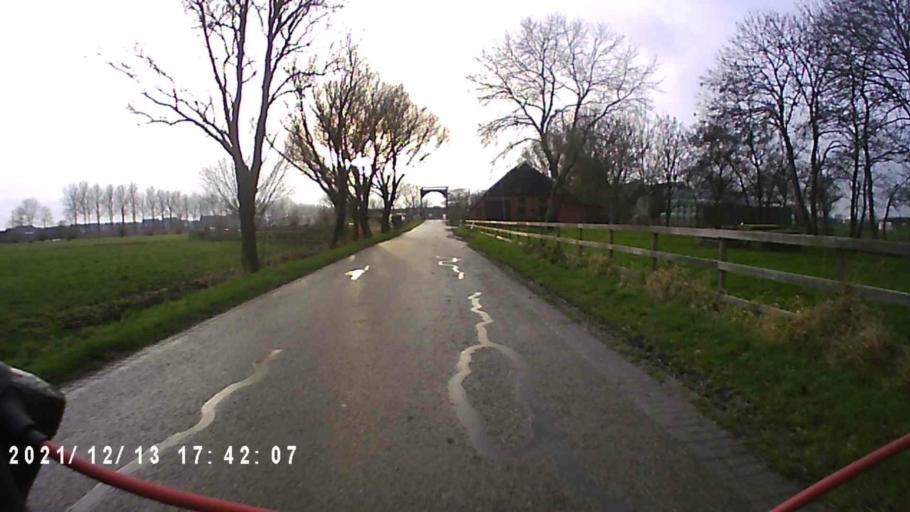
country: NL
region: Groningen
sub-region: Gemeente Bedum
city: Bedum
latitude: 53.2873
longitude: 6.7070
